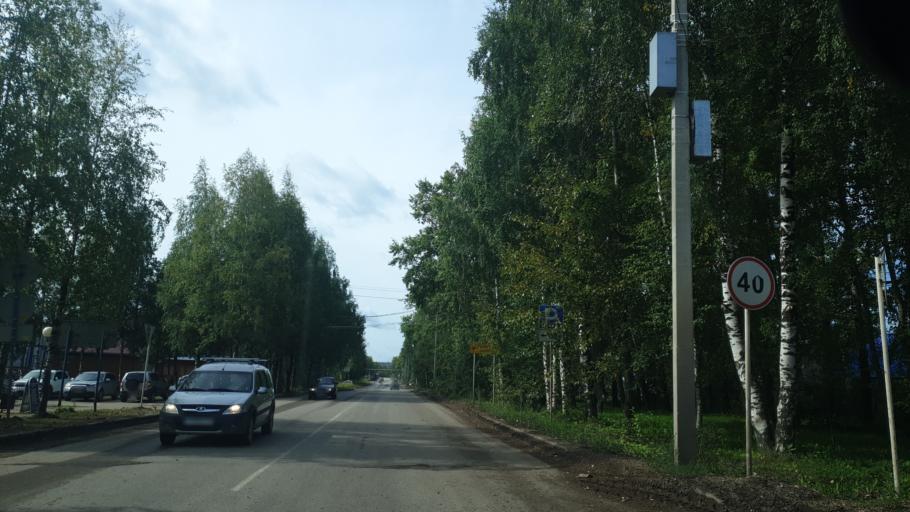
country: RU
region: Komi Republic
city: Ezhva
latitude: 61.8096
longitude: 50.7363
